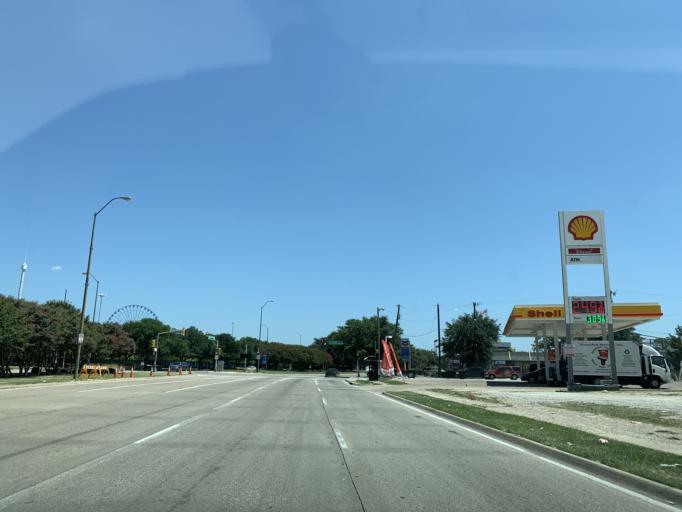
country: US
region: Texas
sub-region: Dallas County
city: Dallas
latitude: 32.7778
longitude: -96.7661
